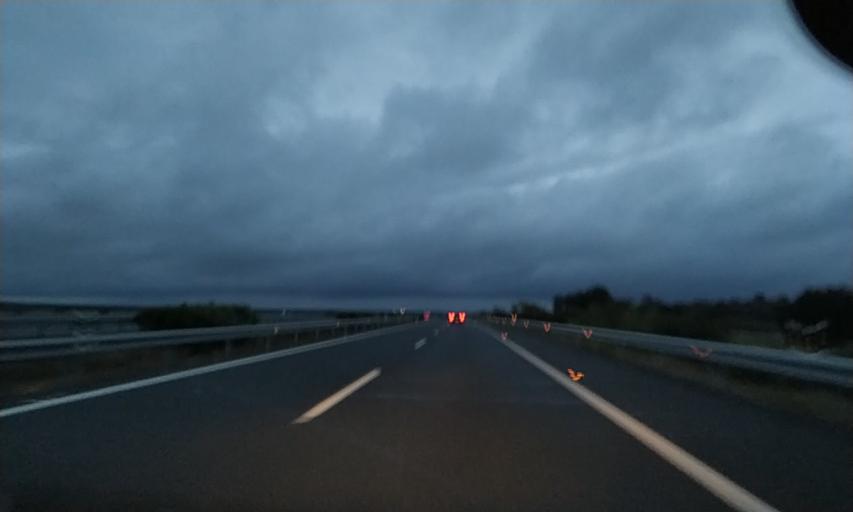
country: ES
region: Extremadura
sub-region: Provincia de Caceres
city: Casas de Don Antonio
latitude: 39.2463
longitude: -6.3061
